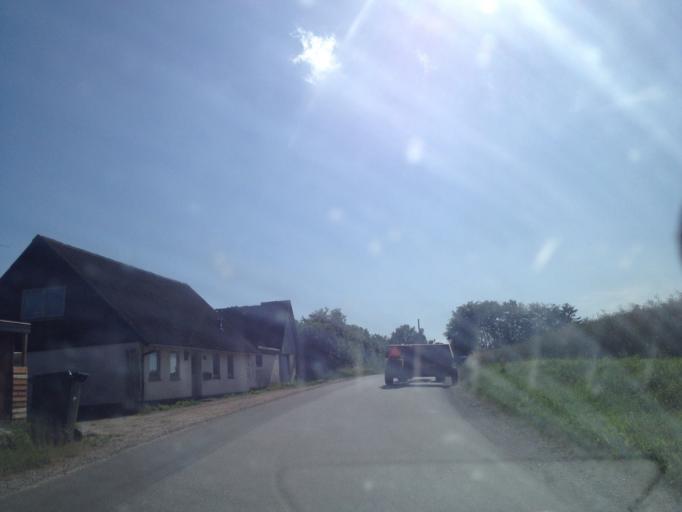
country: DK
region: South Denmark
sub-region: Kolding Kommune
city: Christiansfeld
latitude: 55.3995
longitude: 9.4863
